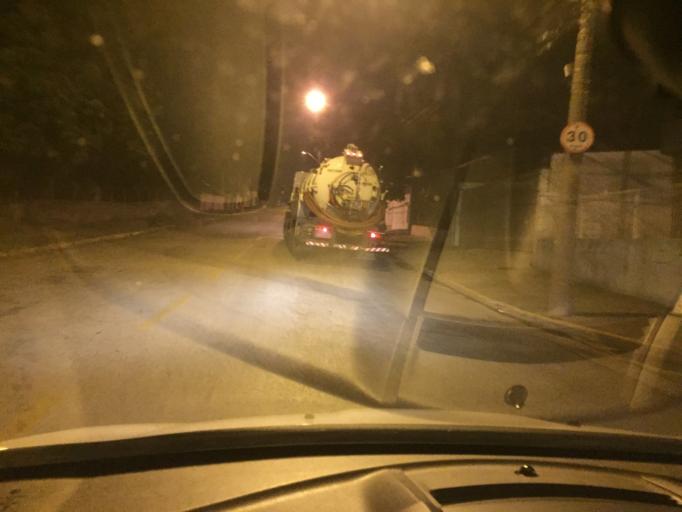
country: BR
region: Sao Paulo
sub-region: Varzea Paulista
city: Varzea Paulista
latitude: -23.2094
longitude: -46.8434
